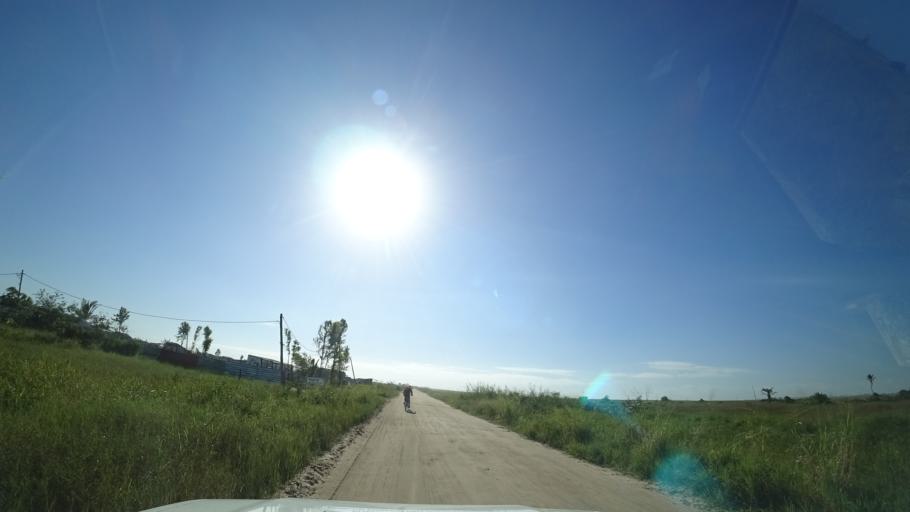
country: MZ
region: Sofala
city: Beira
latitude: -19.7623
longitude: 34.9080
